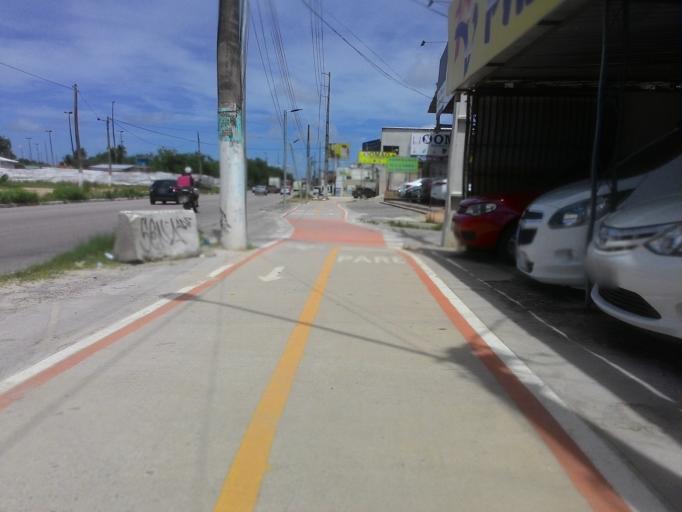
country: BR
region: Pernambuco
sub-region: Olinda
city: Olinda
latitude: -8.0271
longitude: -34.8650
